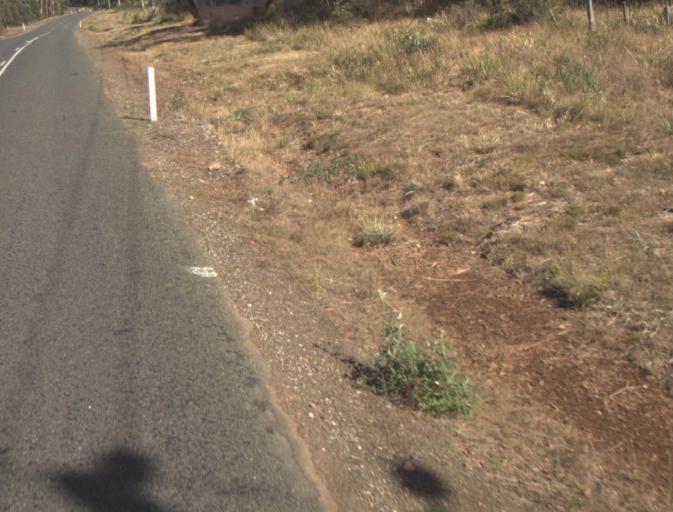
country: AU
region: Tasmania
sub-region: Launceston
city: Mayfield
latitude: -41.3294
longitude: 147.1402
